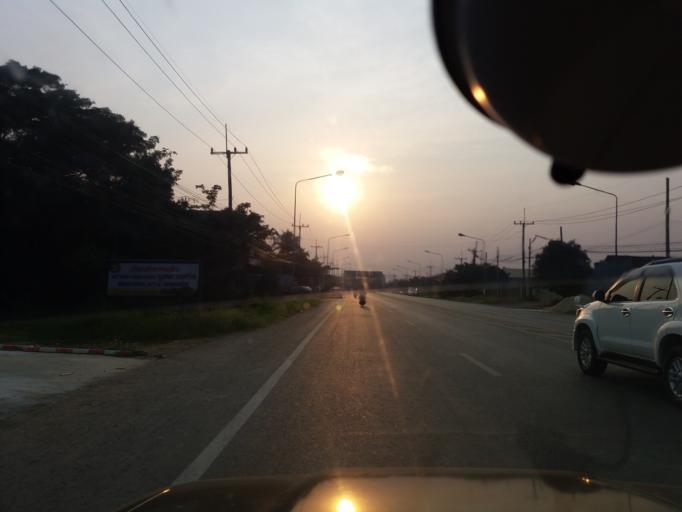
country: TH
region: Sing Buri
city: Sing Buri
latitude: 14.8874
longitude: 100.3948
